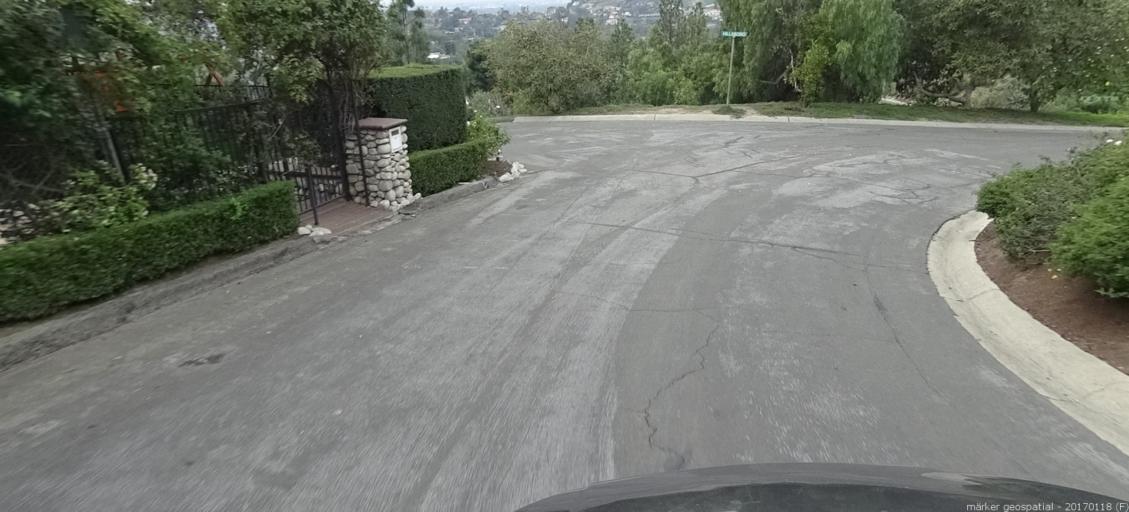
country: US
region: California
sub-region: Orange County
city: North Tustin
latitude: 33.7766
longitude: -117.7814
